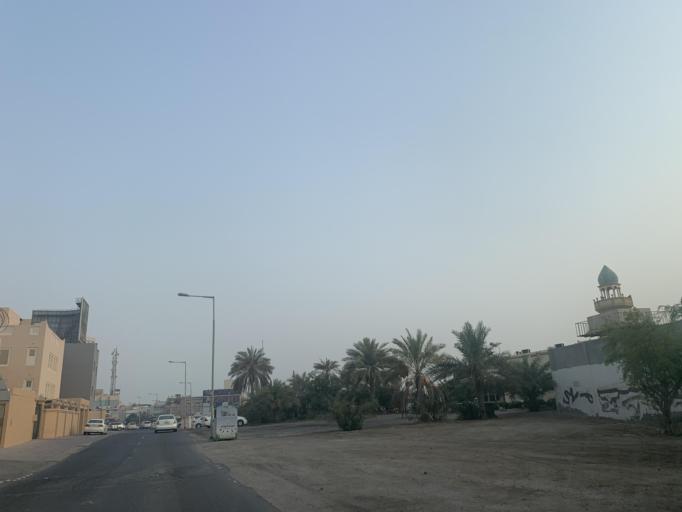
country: BH
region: Manama
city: Jidd Hafs
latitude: 26.2195
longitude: 50.5172
